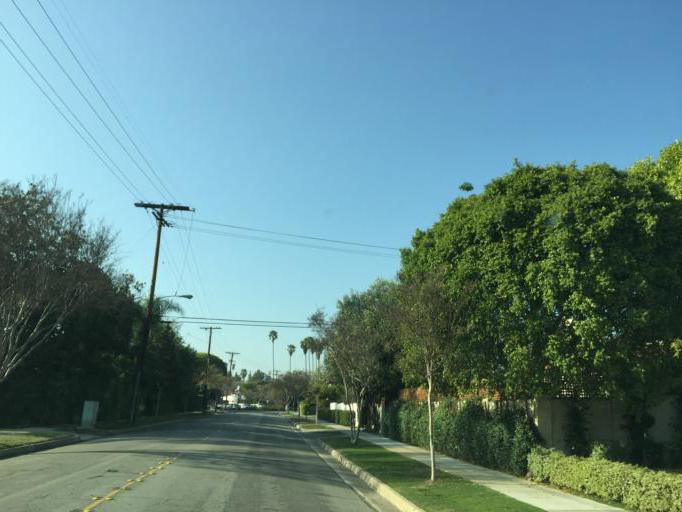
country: US
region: California
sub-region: Los Angeles County
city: South Pasadena
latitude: 34.1149
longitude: -118.1353
